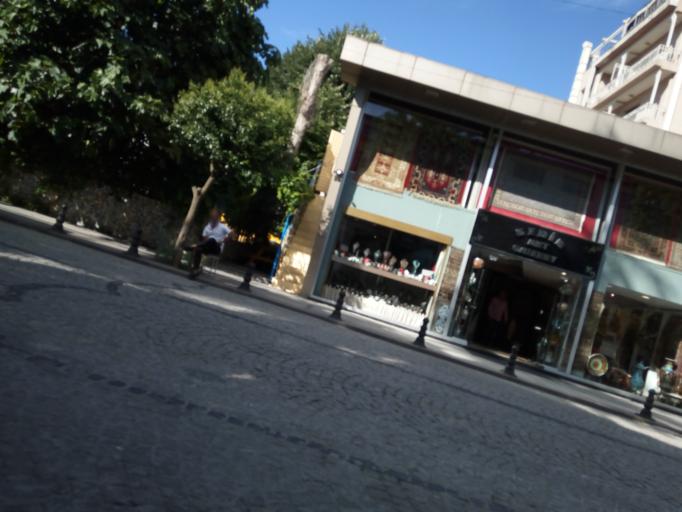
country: TR
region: Istanbul
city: Eminoenue
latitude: 41.0092
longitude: 28.9772
